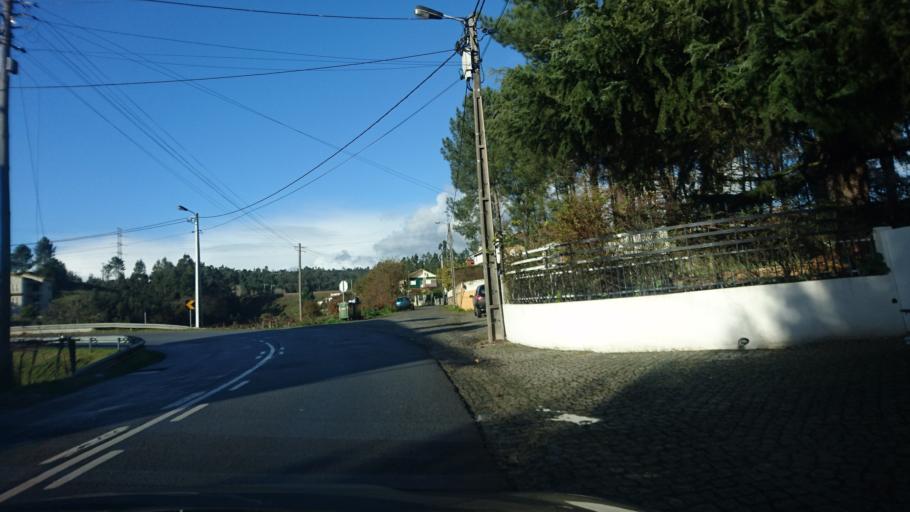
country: PT
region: Porto
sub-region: Paredes
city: Recarei
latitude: 41.1578
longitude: -8.4204
